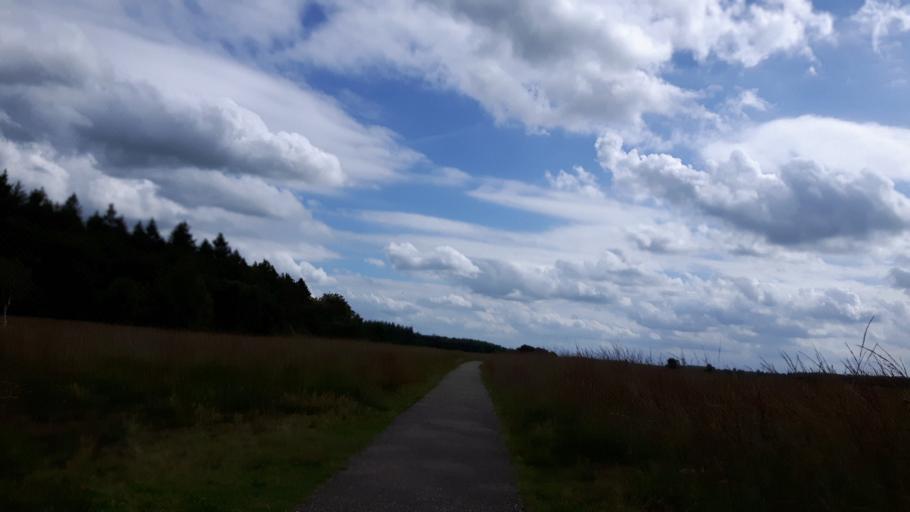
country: NL
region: Friesland
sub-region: Gemeente Smallingerland
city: Drachtstercompagnie
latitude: 53.0620
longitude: 6.2344
